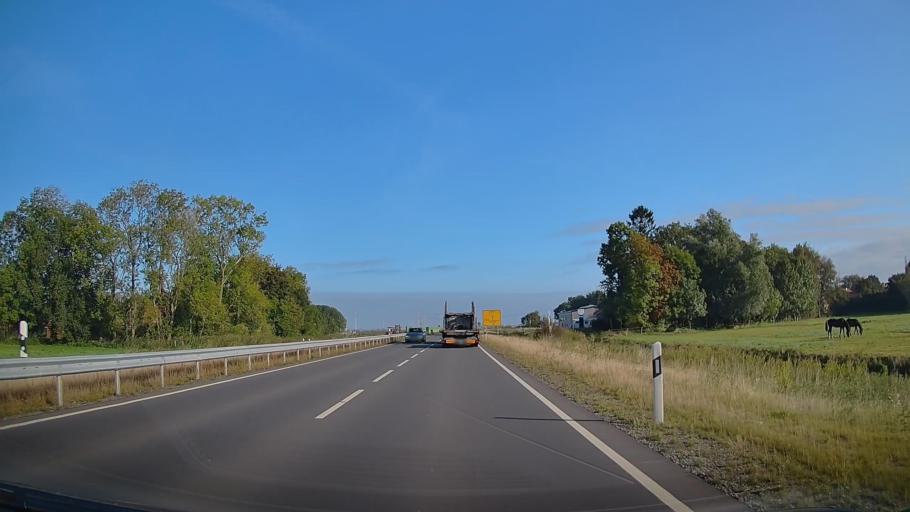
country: DE
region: Lower Saxony
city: Ovelgonne
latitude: 53.3093
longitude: 8.3982
